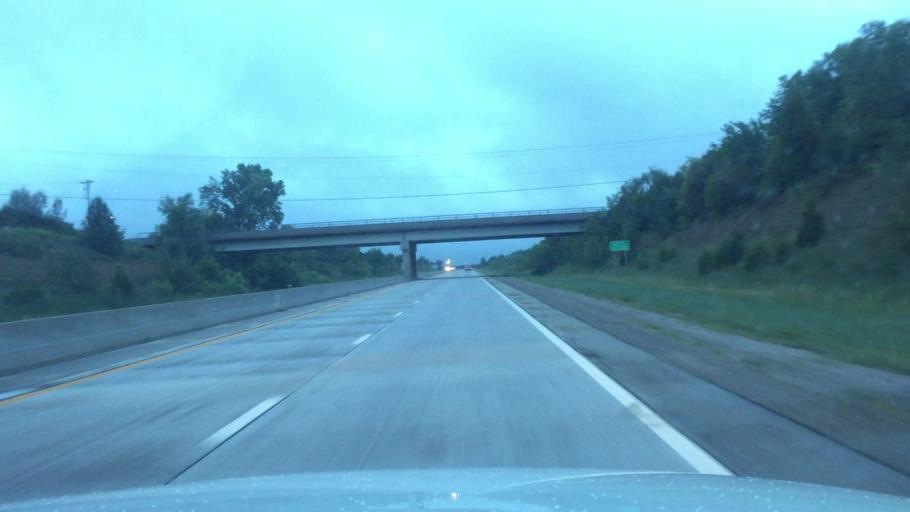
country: US
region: Kansas
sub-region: Neosho County
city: Chanute
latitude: 37.6758
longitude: -95.4796
